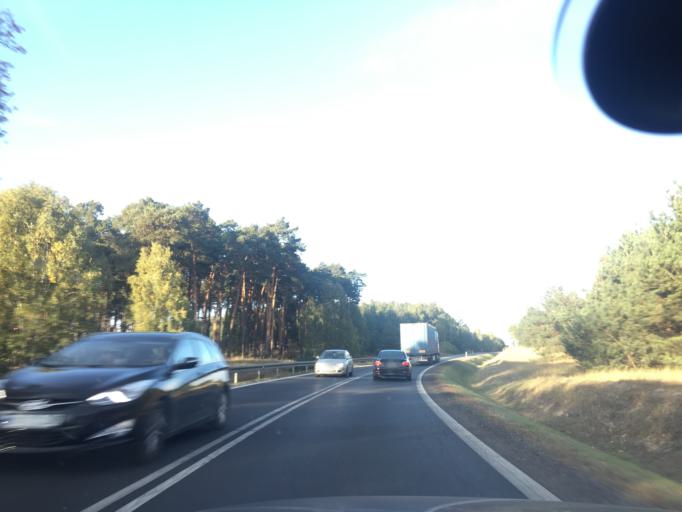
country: PL
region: Kujawsko-Pomorskie
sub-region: Powiat torunski
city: Wielka Nieszawka
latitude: 52.9424
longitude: 18.5187
